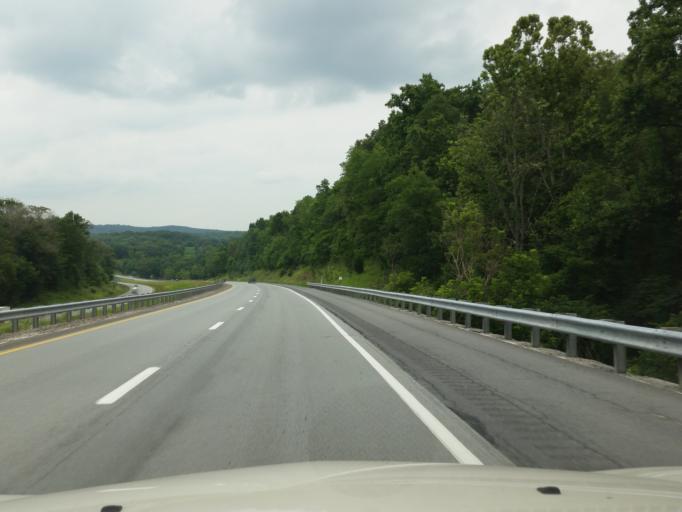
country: US
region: Pennsylvania
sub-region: Perry County
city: Newport
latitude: 40.5092
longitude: -77.1269
